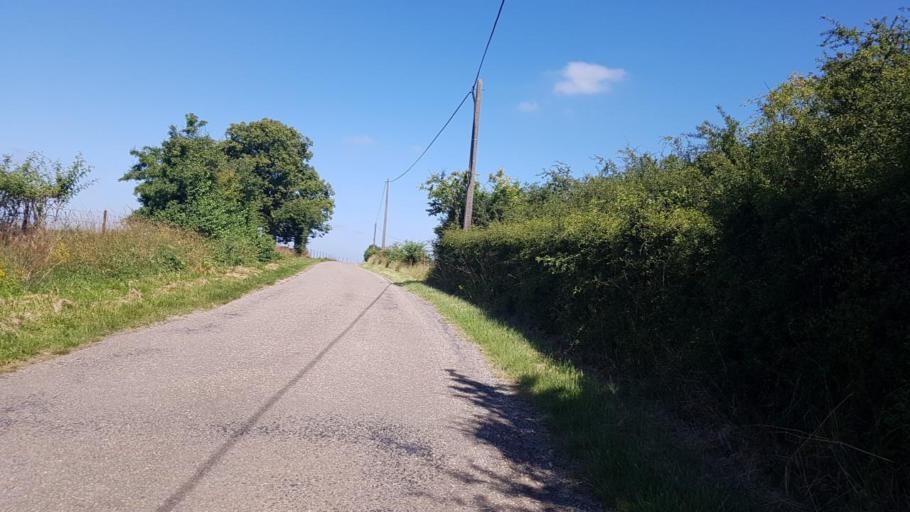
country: BE
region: Wallonia
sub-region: Province du Hainaut
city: Chimay
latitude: 50.0625
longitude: 4.2417
